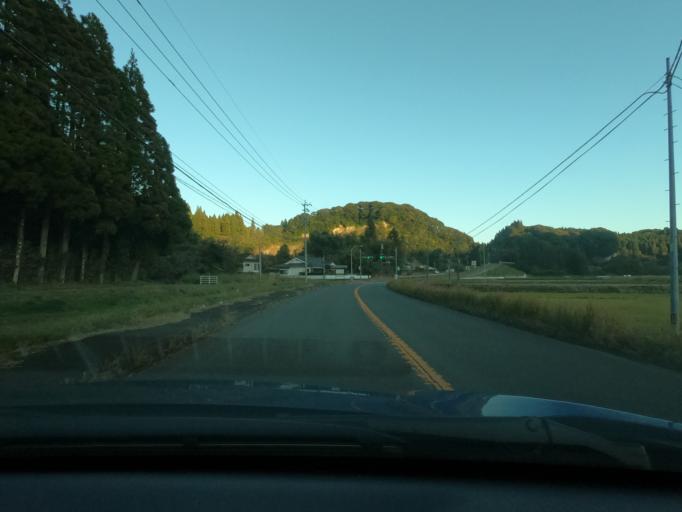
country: JP
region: Kagoshima
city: Satsumasendai
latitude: 31.8075
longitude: 130.3885
